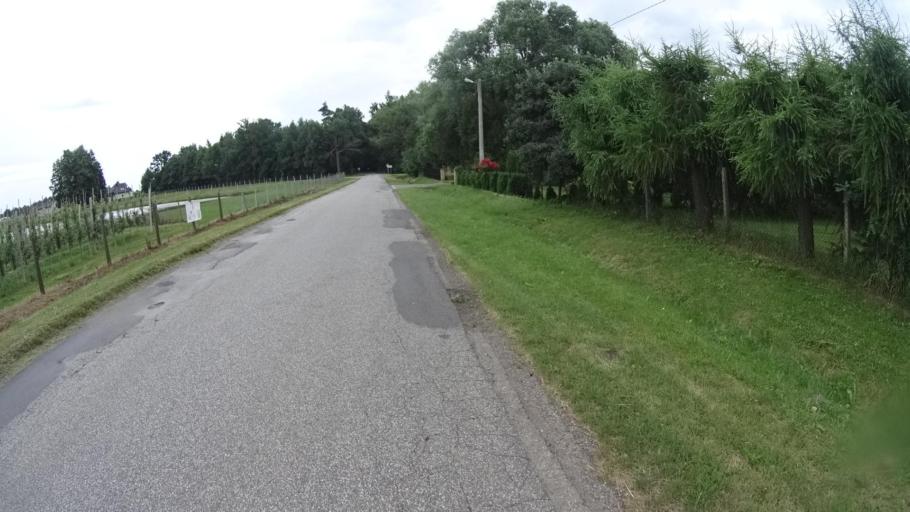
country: PL
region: Masovian Voivodeship
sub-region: Powiat grojecki
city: Goszczyn
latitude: 51.7833
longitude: 20.8545
